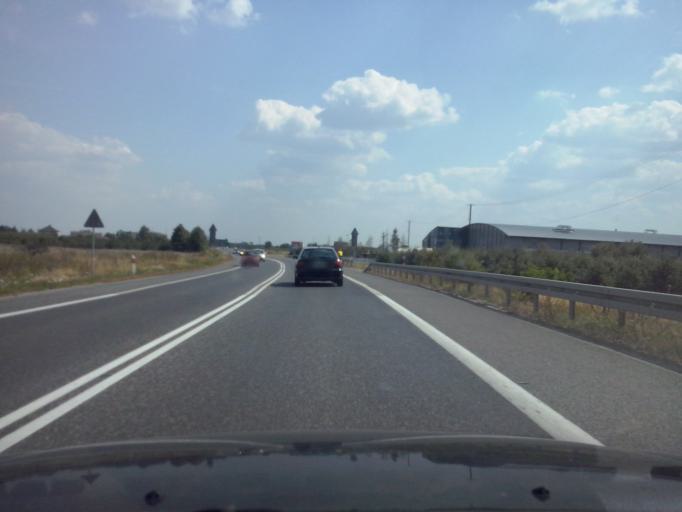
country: PL
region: Swietokrzyskie
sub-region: Powiat sandomierski
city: Loniow
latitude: 50.5461
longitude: 21.5509
